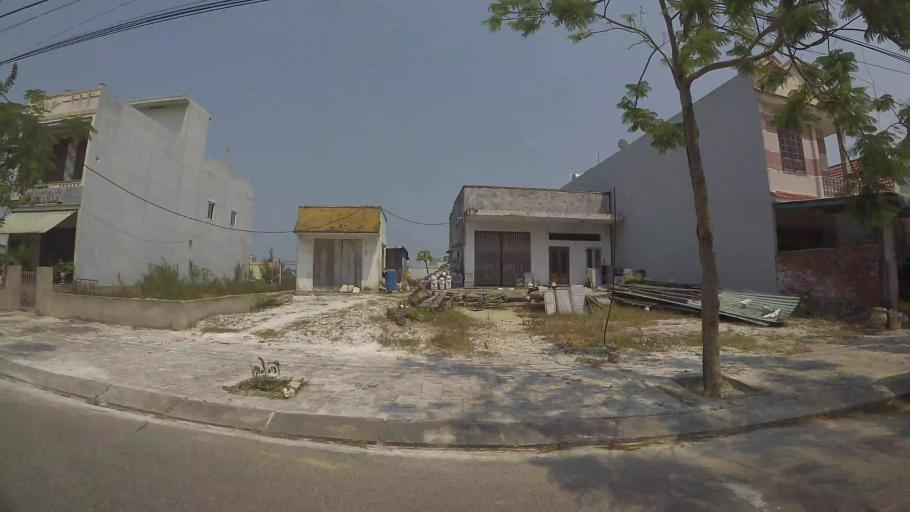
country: VN
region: Da Nang
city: Ngu Hanh Son
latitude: 15.9910
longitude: 108.2668
